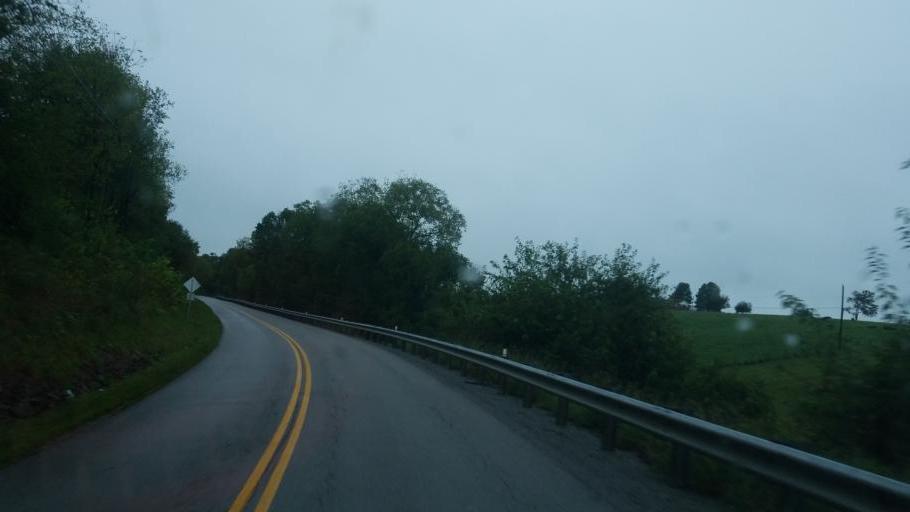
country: US
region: Kentucky
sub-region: Fleming County
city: Flemingsburg
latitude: 38.4176
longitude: -83.6972
